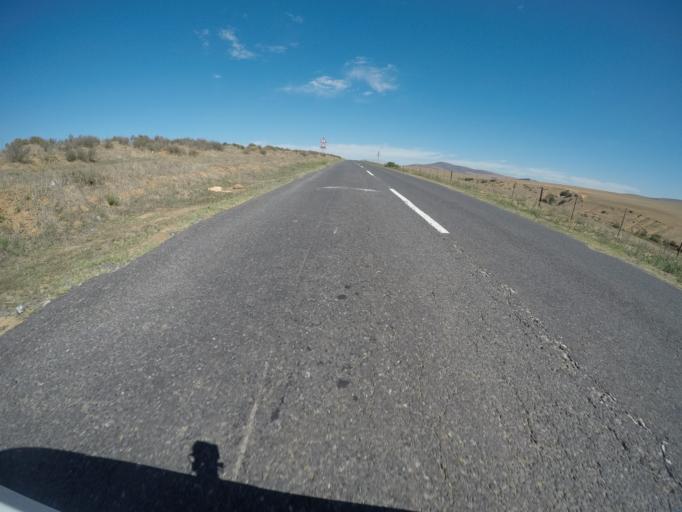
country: ZA
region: Western Cape
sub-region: City of Cape Town
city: Atlantis
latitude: -33.6794
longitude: 18.6036
